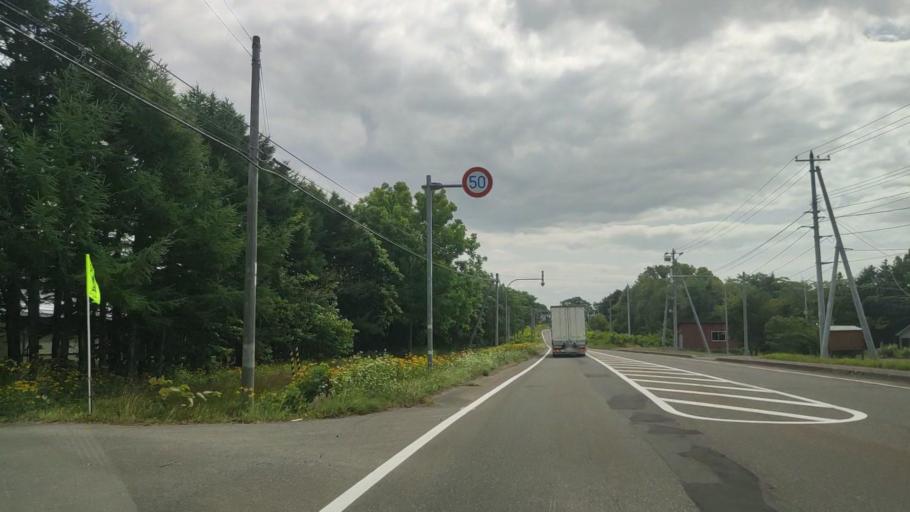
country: JP
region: Hokkaido
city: Rumoi
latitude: 44.5623
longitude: 141.7858
